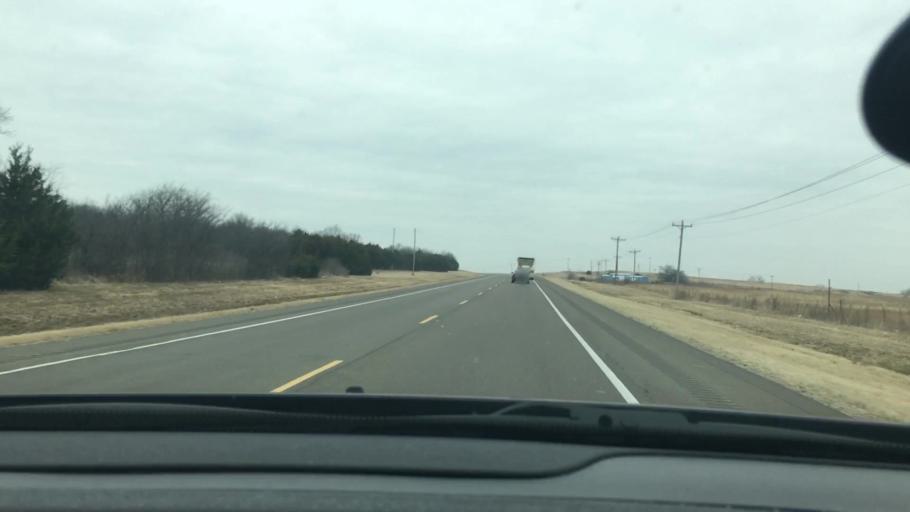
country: US
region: Oklahoma
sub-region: Murray County
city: Davis
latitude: 34.5171
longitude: -97.2067
